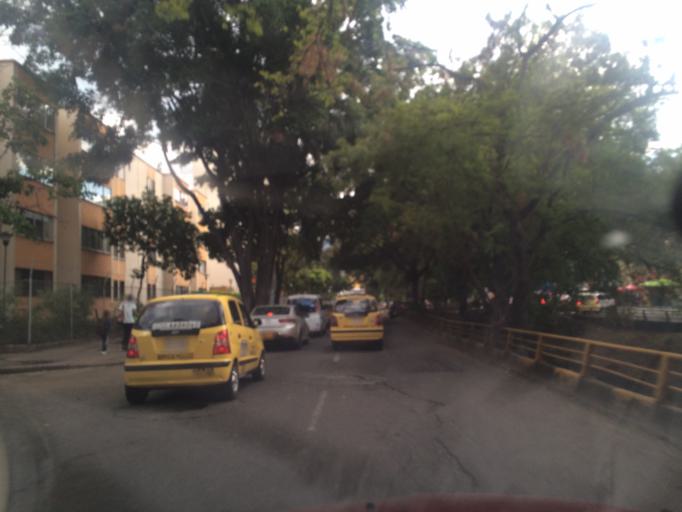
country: CO
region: Valle del Cauca
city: Cali
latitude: 3.4216
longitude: -76.5399
